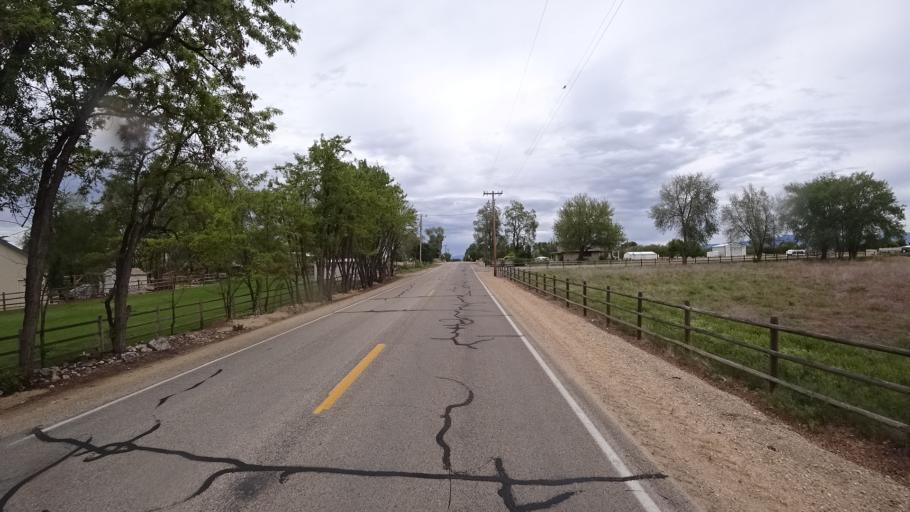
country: US
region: Idaho
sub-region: Ada County
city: Kuna
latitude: 43.5532
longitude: -116.4140
